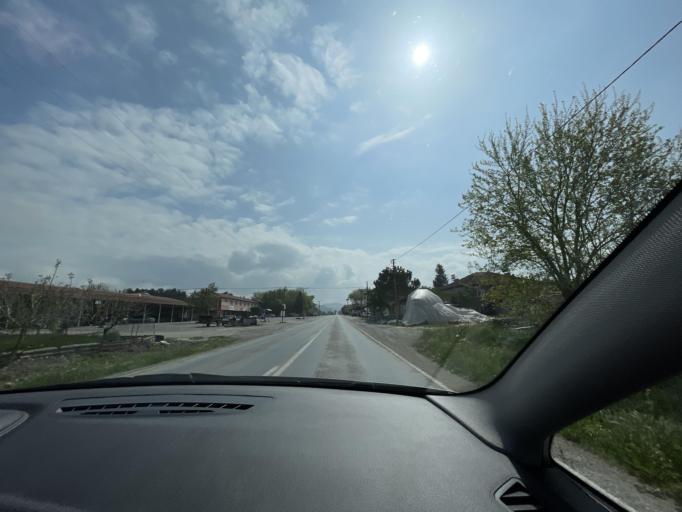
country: TR
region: Denizli
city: Acipayam
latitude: 37.5080
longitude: 29.4016
